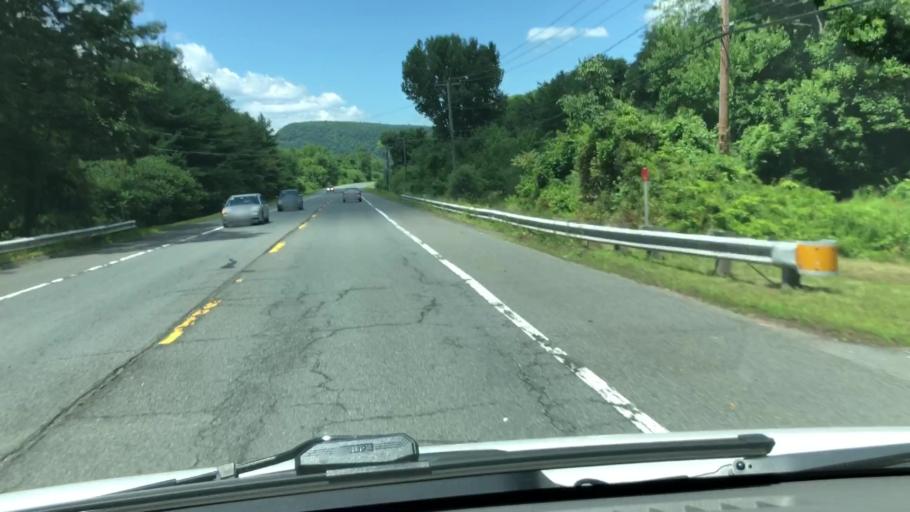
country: US
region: Massachusetts
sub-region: Franklin County
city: South Deerfield
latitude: 42.4576
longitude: -72.5694
